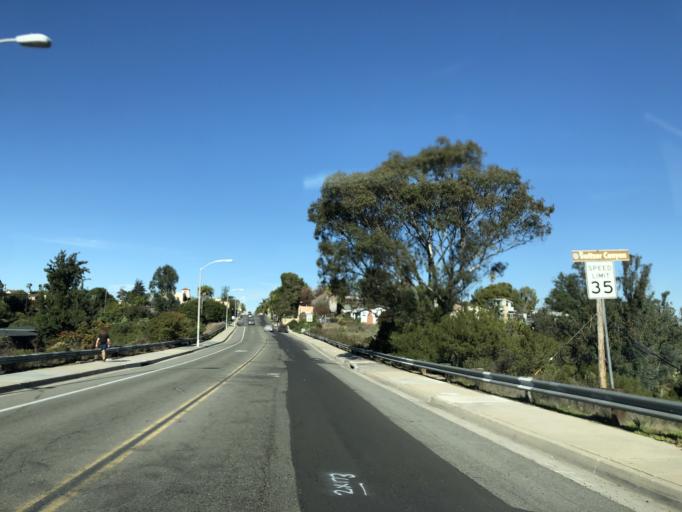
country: US
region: California
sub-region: San Diego County
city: San Diego
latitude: 32.7331
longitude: -117.1294
